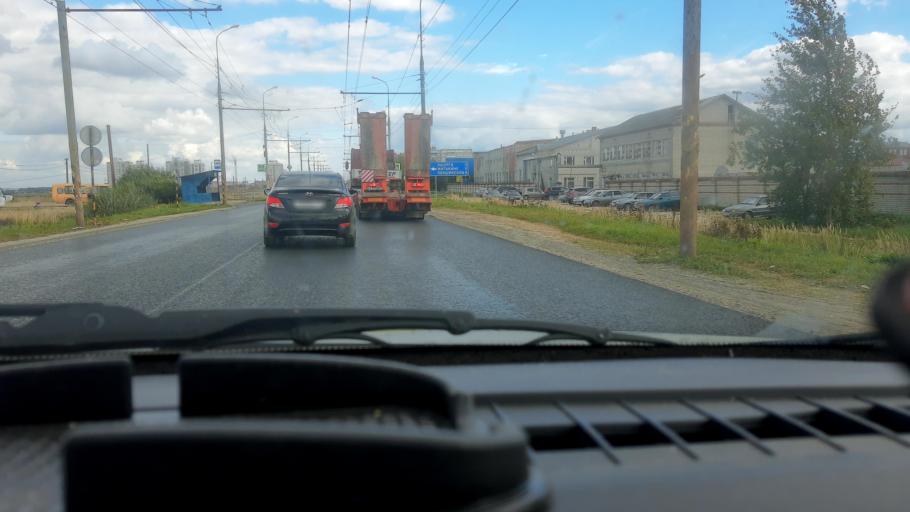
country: RU
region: Mariy-El
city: Medvedevo
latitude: 56.6385
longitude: 47.7851
